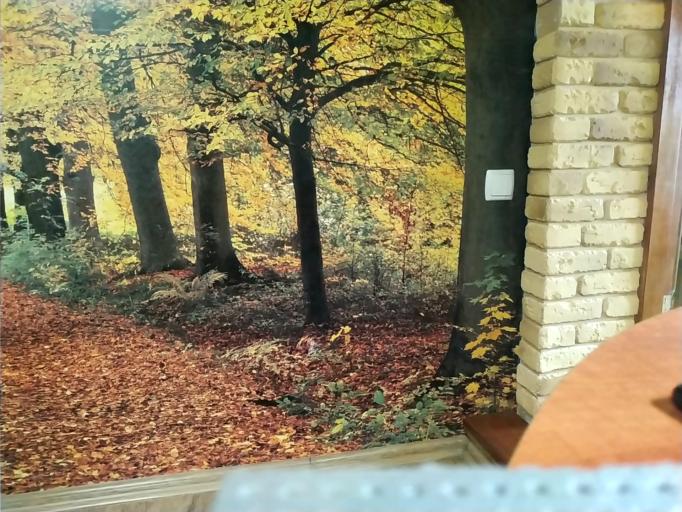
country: RU
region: Tverskaya
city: Likhoslavl'
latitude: 56.9866
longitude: 35.3886
